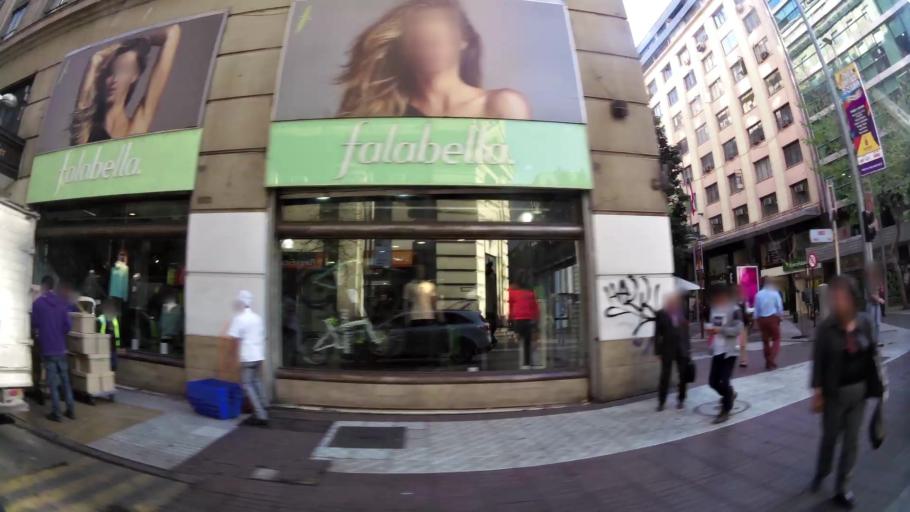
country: CL
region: Santiago Metropolitan
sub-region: Provincia de Santiago
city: Santiago
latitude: -33.4419
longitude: -70.6508
